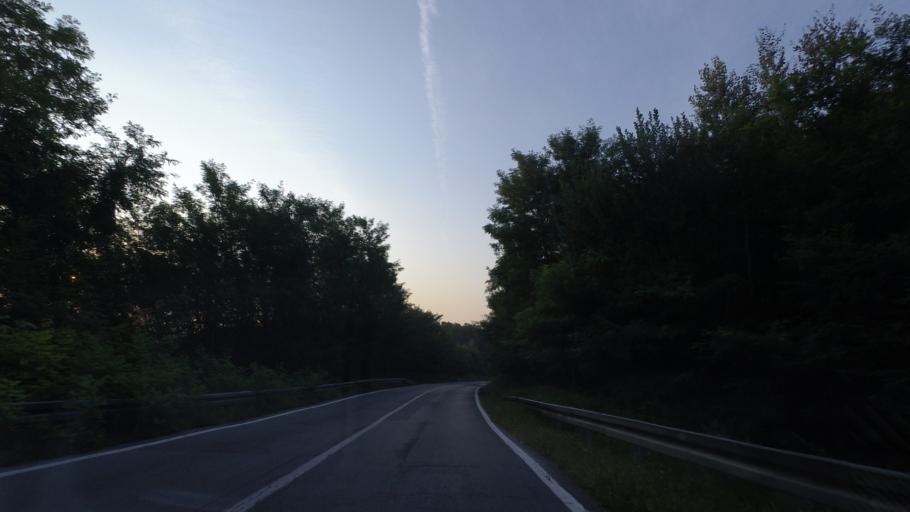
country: HR
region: Brodsko-Posavska
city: Cernik
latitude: 45.2858
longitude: 17.4114
